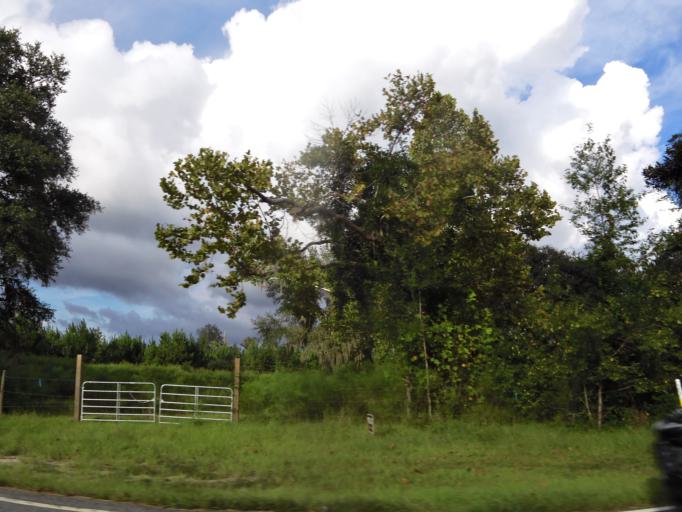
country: US
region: Georgia
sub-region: Liberty County
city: Midway
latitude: 31.8599
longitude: -81.4306
